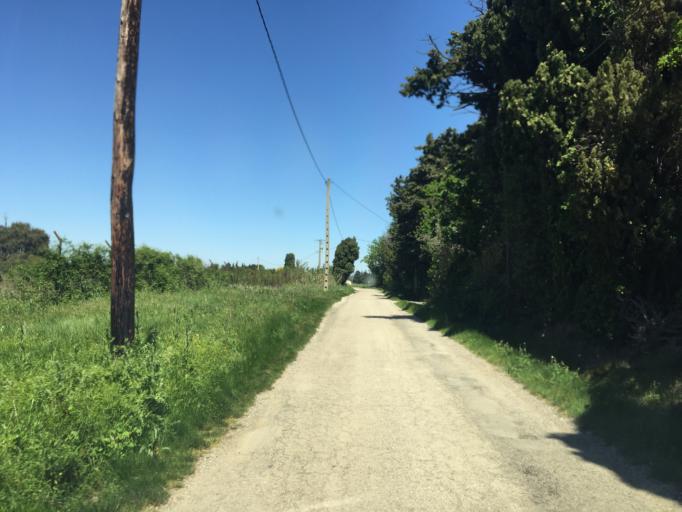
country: FR
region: Provence-Alpes-Cote d'Azur
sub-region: Departement du Vaucluse
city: Jonquieres
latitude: 44.1364
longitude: 4.9148
